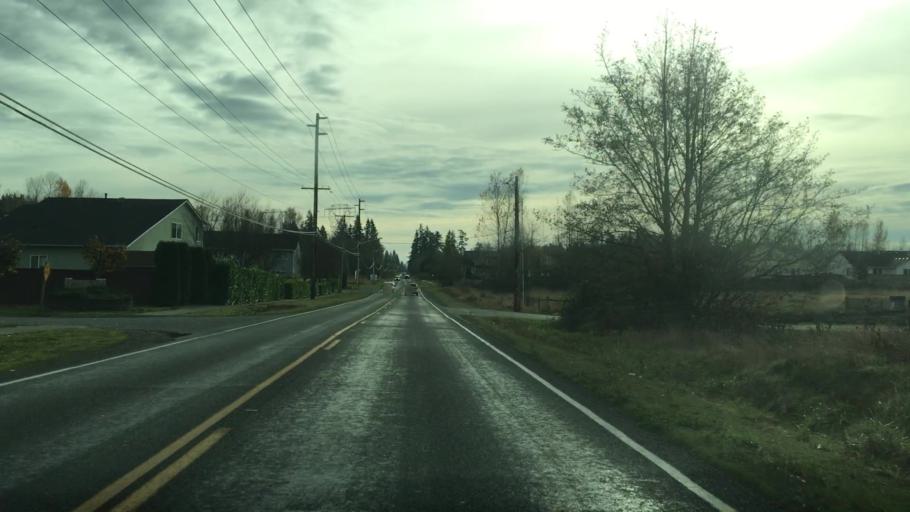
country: US
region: Washington
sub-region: Pierce County
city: South Hill
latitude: 47.1343
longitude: -122.3149
